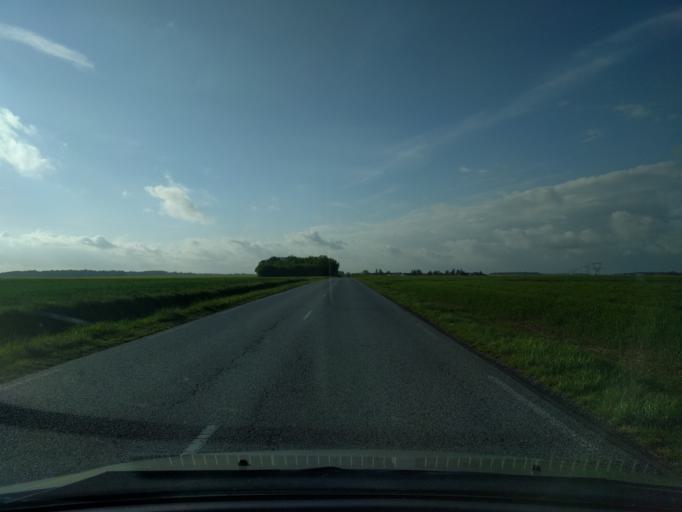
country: FR
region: Haute-Normandie
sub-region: Departement de l'Eure
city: Damville
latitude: 48.9000
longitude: 1.0322
